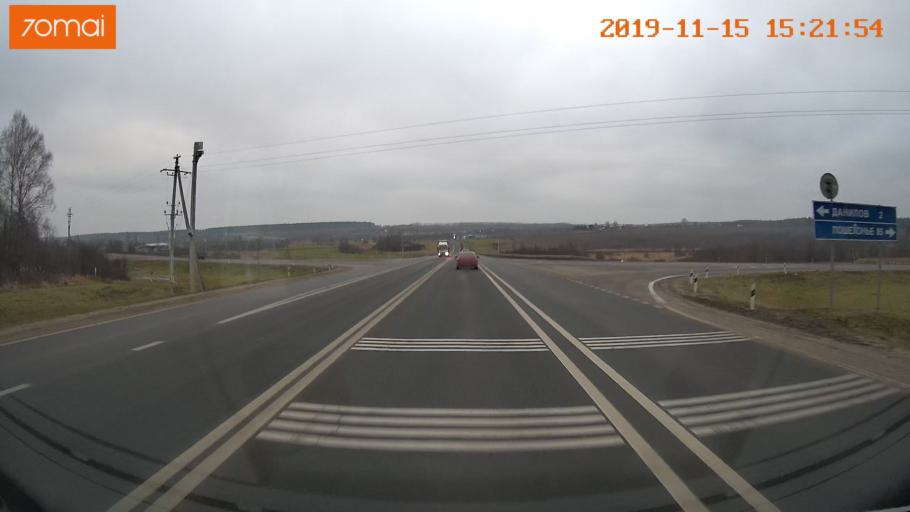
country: RU
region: Jaroslavl
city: Danilov
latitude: 58.2083
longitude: 40.1394
